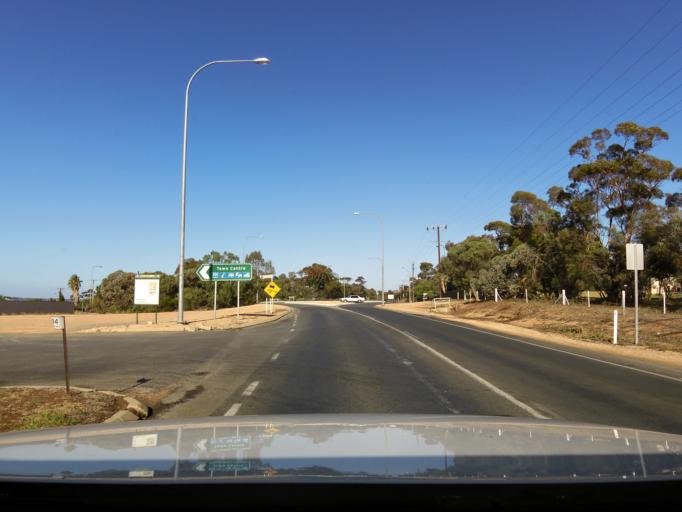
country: AU
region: South Australia
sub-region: Berri and Barmera
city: Berri
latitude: -34.2718
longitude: 140.6074
